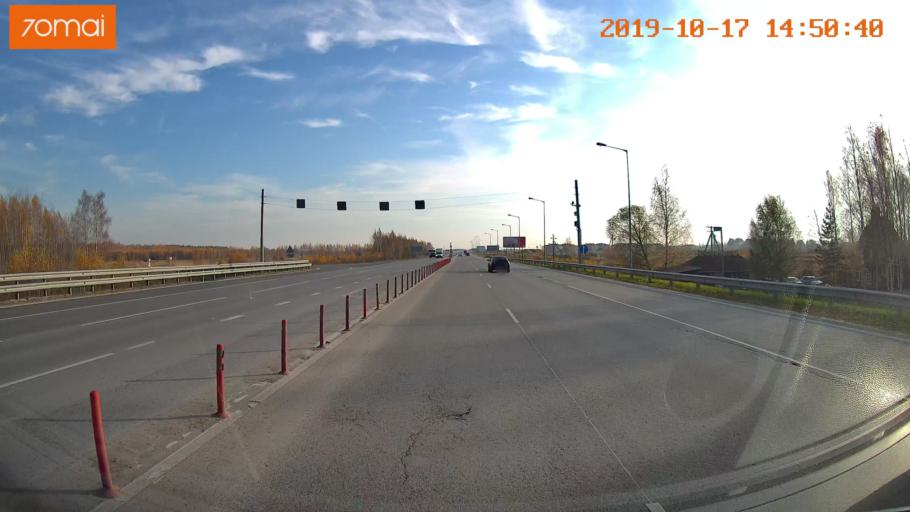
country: RU
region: Rjazan
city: Polyany
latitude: 54.7308
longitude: 39.8438
